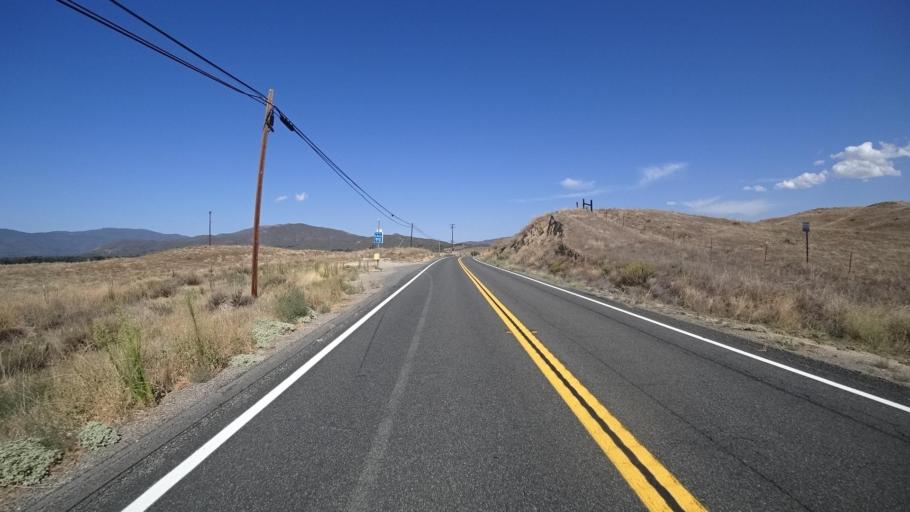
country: US
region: California
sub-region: Riverside County
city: Aguanga
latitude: 33.2957
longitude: -116.6875
